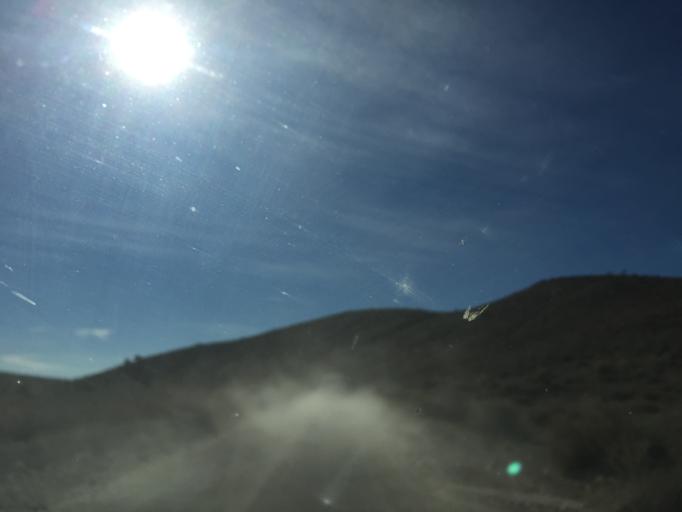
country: US
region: California
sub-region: Inyo County
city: Lone Pine
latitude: 36.8710
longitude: -117.4990
